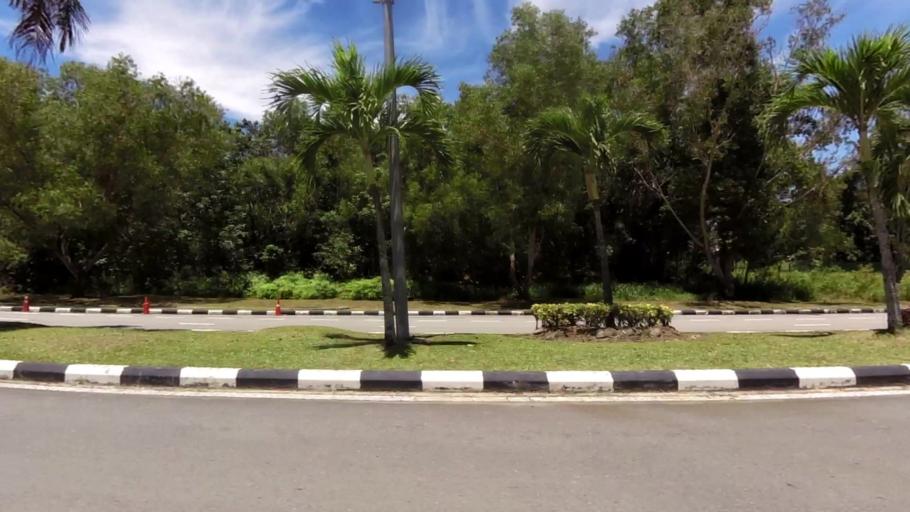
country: BN
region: Brunei and Muara
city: Bandar Seri Begawan
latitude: 4.9220
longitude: 114.9404
